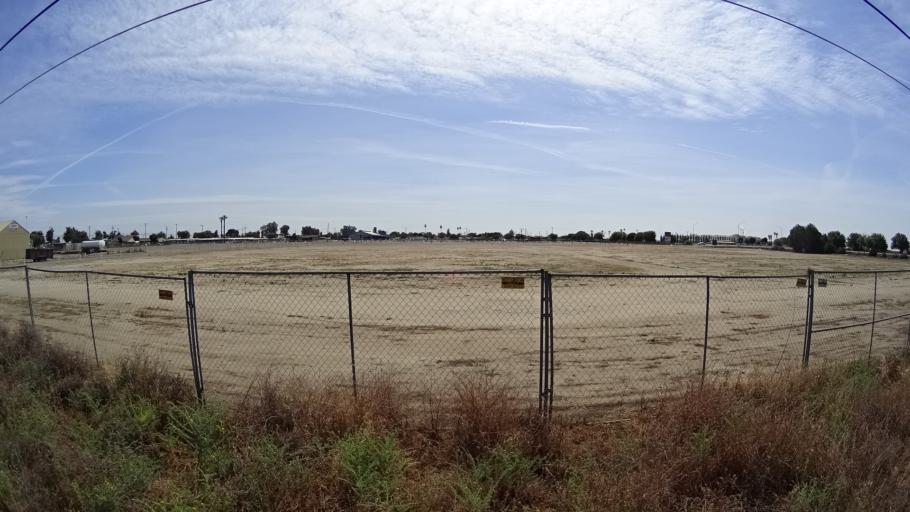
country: US
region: California
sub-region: Kings County
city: Hanford
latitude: 36.3258
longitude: -119.6212
